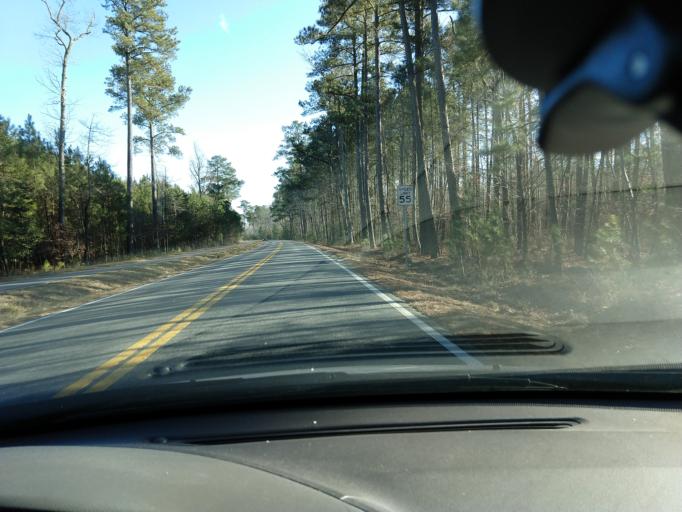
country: US
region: Virginia
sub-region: Charles City County
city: Charles City
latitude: 37.3085
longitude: -76.9621
